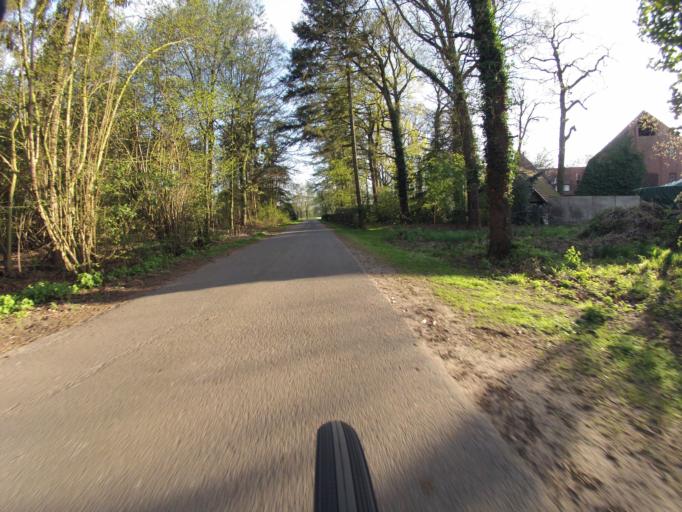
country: DE
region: Lower Saxony
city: Salzbergen
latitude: 52.3322
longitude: 7.3587
